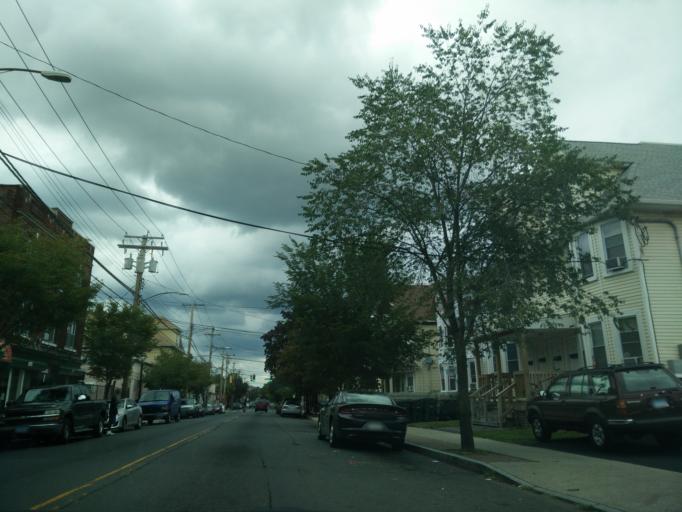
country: US
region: Connecticut
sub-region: Fairfield County
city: Bridgeport
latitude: 41.1926
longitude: -73.1804
